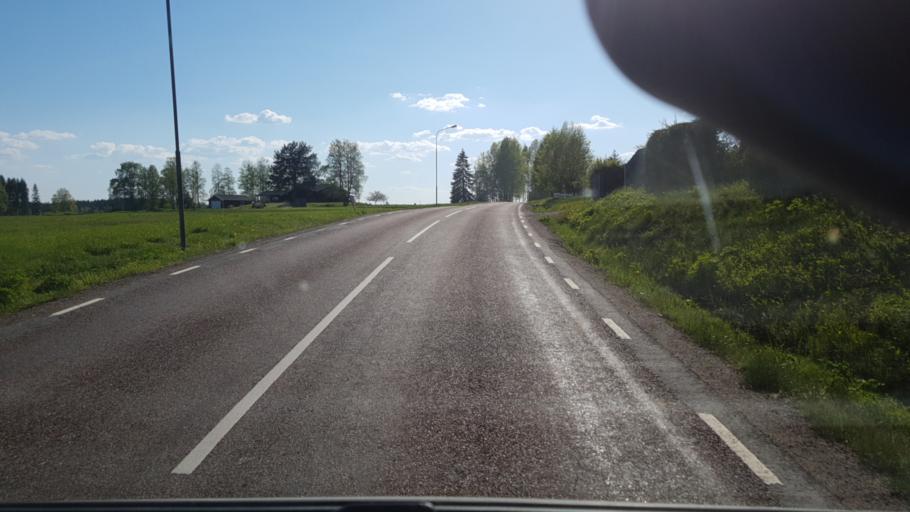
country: SE
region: Vaermland
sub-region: Eda Kommun
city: Charlottenberg
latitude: 59.8864
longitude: 12.3305
